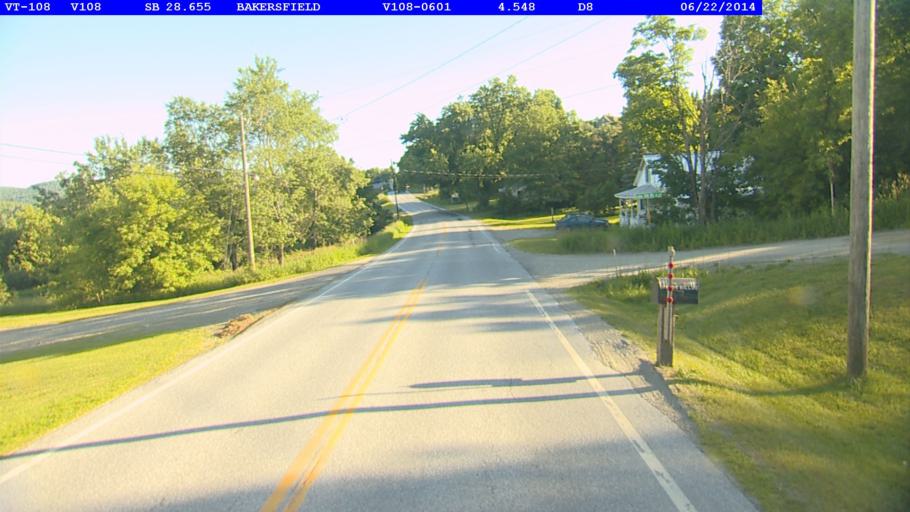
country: US
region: Vermont
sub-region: Franklin County
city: Enosburg Falls
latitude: 44.7942
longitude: -72.7971
